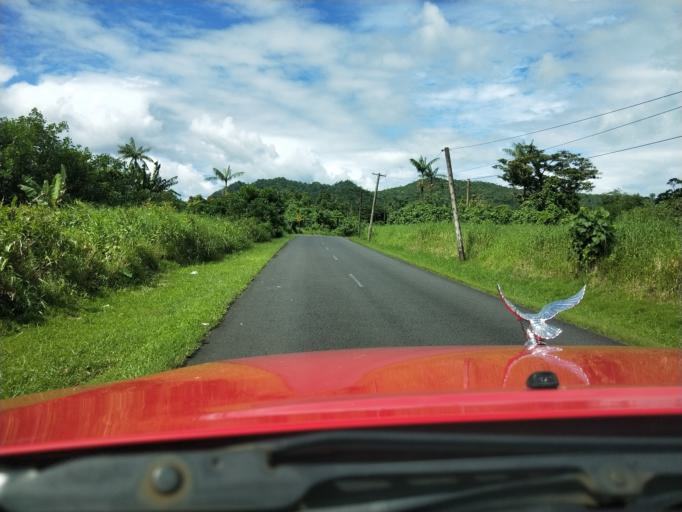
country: WS
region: Va`a-o-Fonoti
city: Samamea
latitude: -13.9633
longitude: -171.5834
